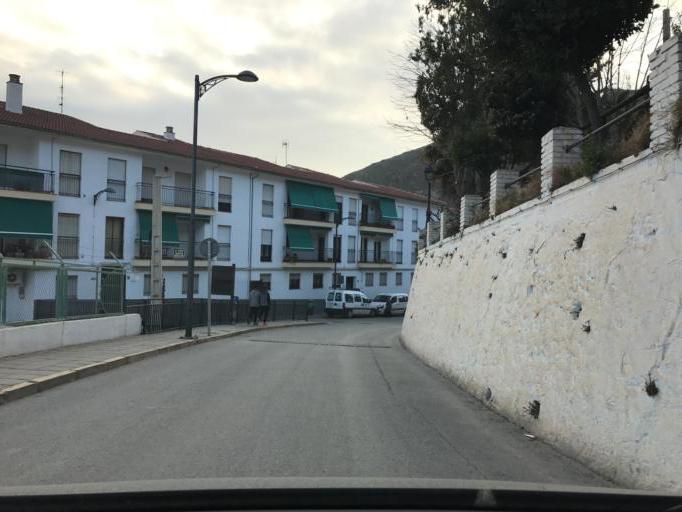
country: ES
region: Andalusia
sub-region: Provincia de Granada
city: Guejar-Sierra
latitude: 37.1589
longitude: -3.4400
